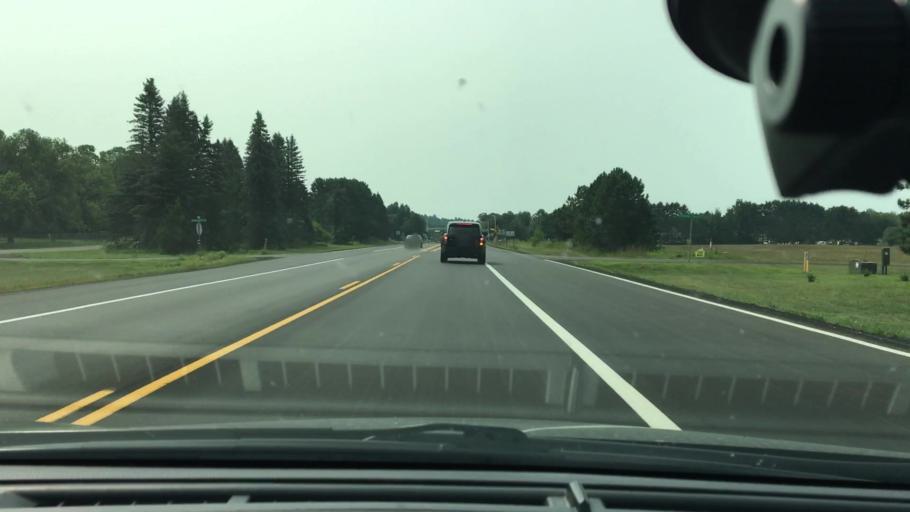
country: US
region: Minnesota
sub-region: Crow Wing County
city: Brainerd
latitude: 46.4024
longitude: -94.1763
